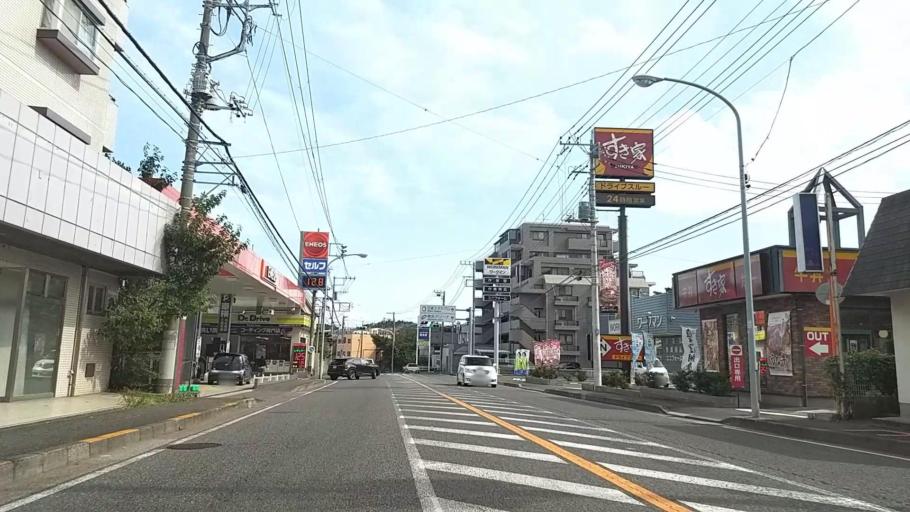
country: JP
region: Kanagawa
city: Yokohama
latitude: 35.5097
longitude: 139.5863
